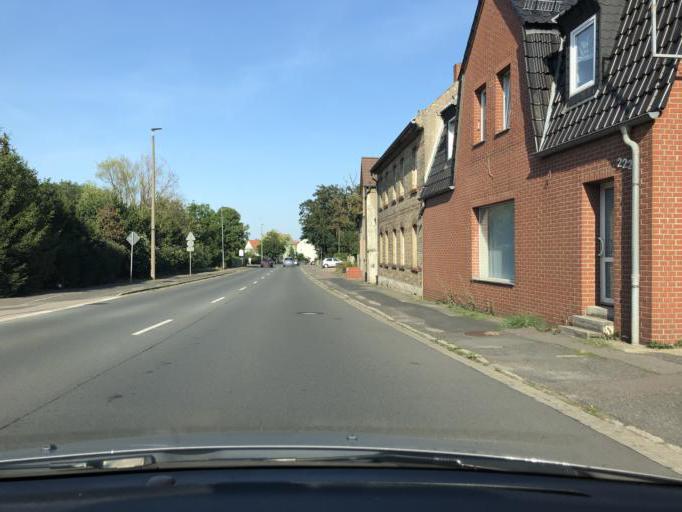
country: DE
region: Saxony-Anhalt
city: Zscherben
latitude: 51.3241
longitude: 11.9640
